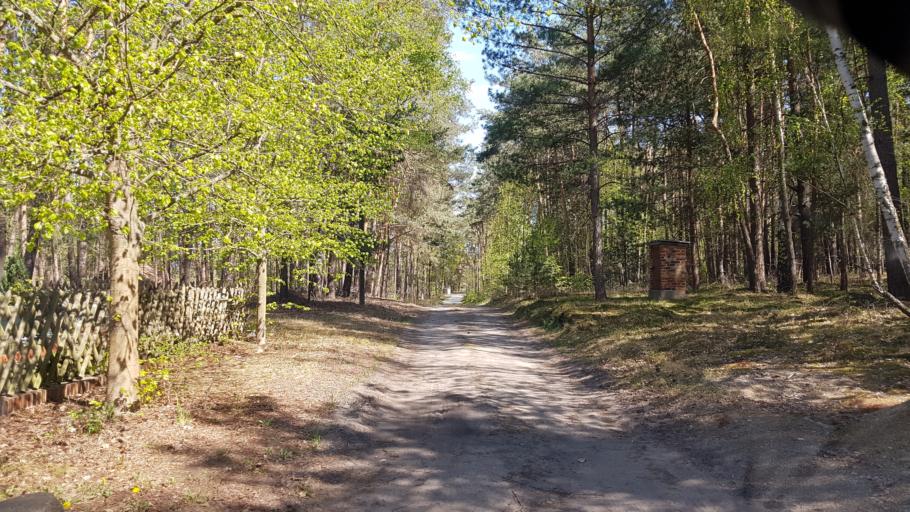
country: DE
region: Brandenburg
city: Crinitz
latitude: 51.7475
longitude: 13.7662
